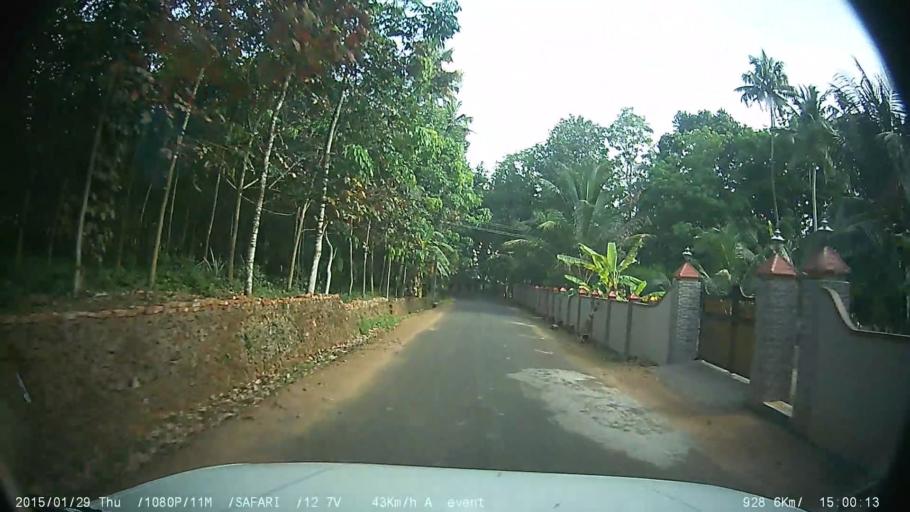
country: IN
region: Kerala
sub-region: Kottayam
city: Palackattumala
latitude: 9.7287
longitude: 76.5651
